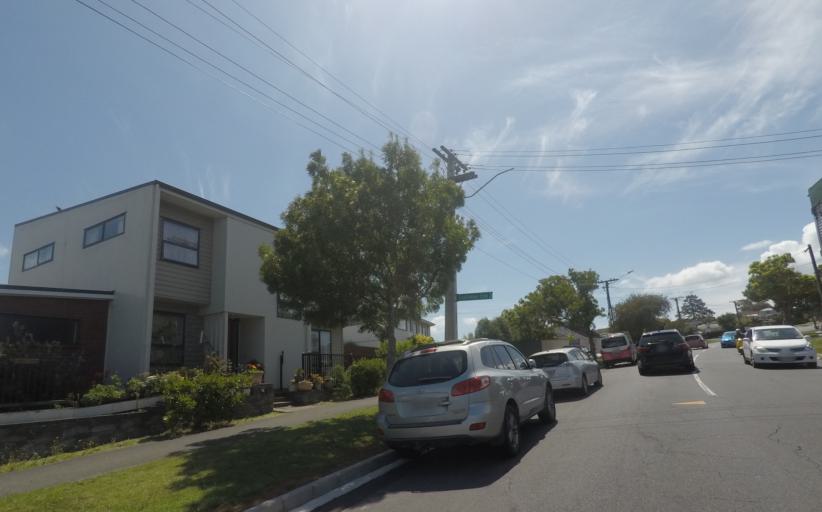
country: NZ
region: Auckland
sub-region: Auckland
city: Tamaki
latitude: -36.8705
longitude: 174.8505
